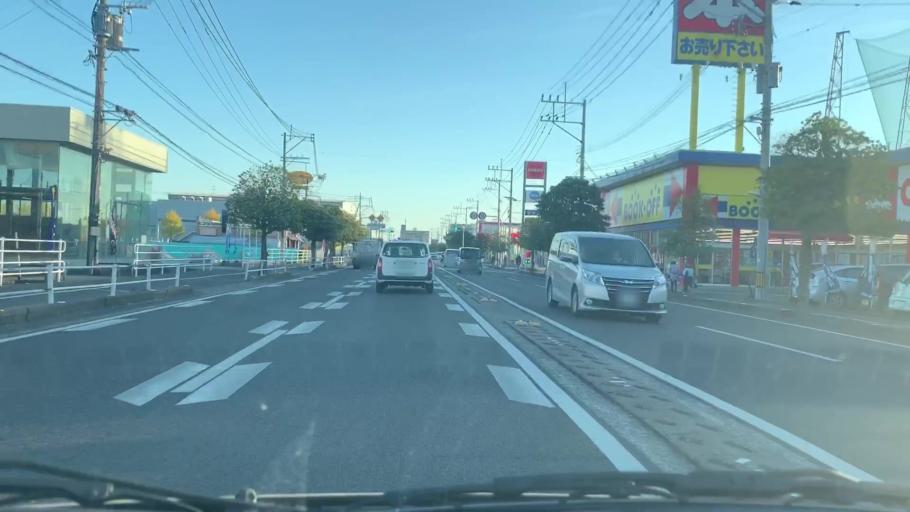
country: JP
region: Saga Prefecture
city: Saga-shi
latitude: 33.2655
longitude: 130.2720
